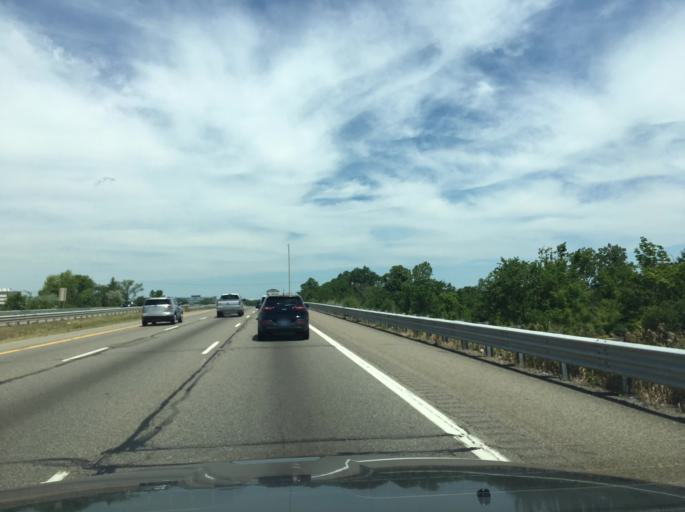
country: US
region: Michigan
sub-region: Oakland County
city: Troy
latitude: 42.5892
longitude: -83.1591
